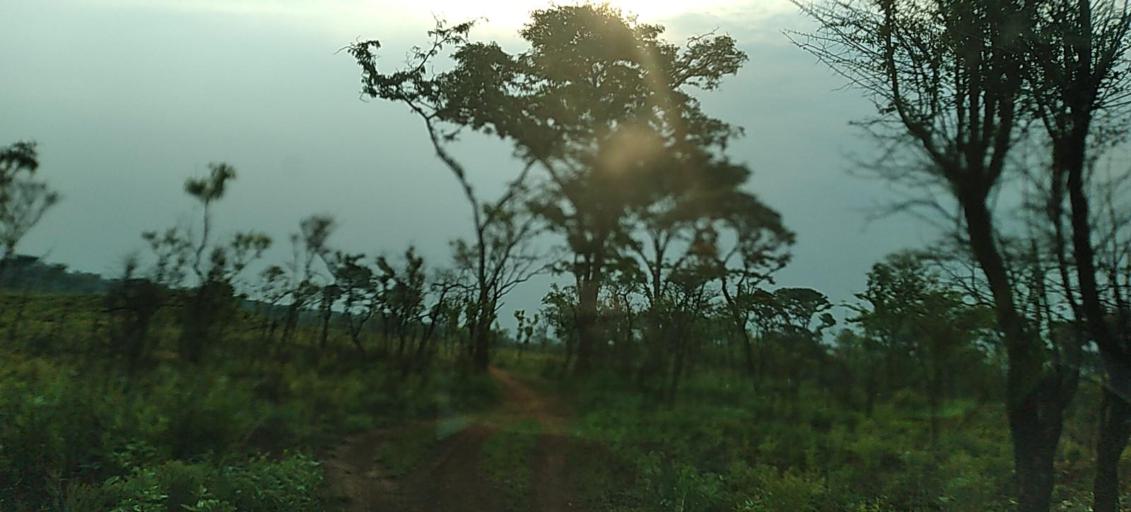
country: ZM
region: North-Western
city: Solwezi
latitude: -12.0424
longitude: 26.0325
